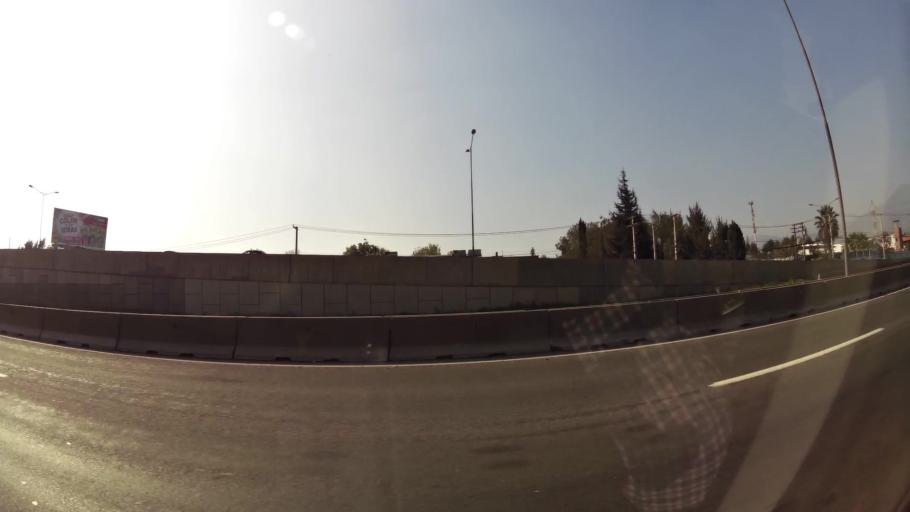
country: CL
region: Santiago Metropolitan
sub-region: Provincia de Santiago
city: Lo Prado
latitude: -33.3660
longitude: -70.6977
